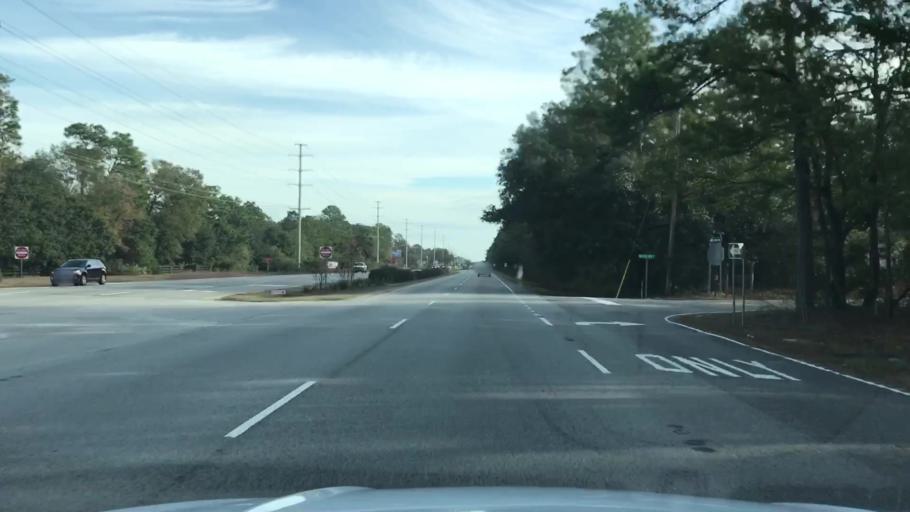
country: US
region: South Carolina
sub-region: Georgetown County
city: Georgetown
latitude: 33.4206
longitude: -79.1743
